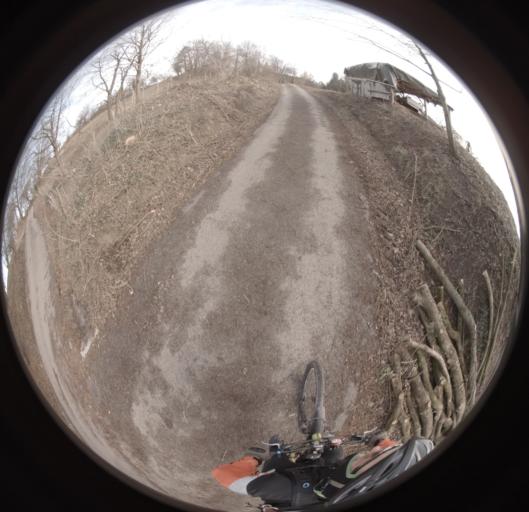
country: DE
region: Baden-Wuerttemberg
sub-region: Regierungsbezirk Stuttgart
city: Waschenbeuren
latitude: 48.7394
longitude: 9.6991
